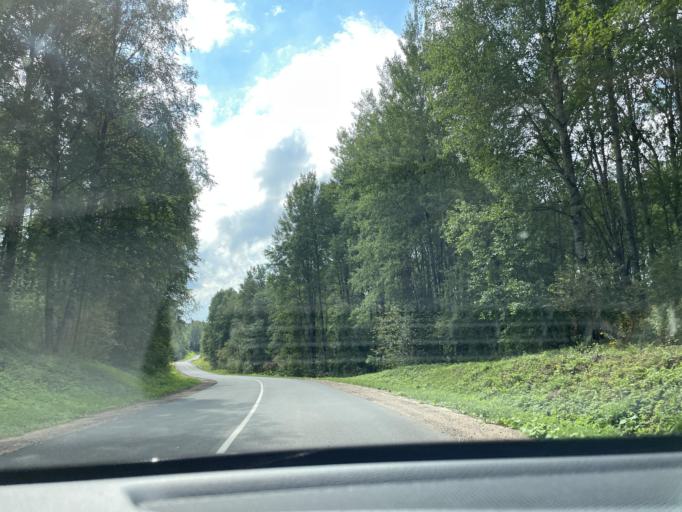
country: RU
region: Novgorod
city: Valday
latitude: 58.0116
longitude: 33.1769
